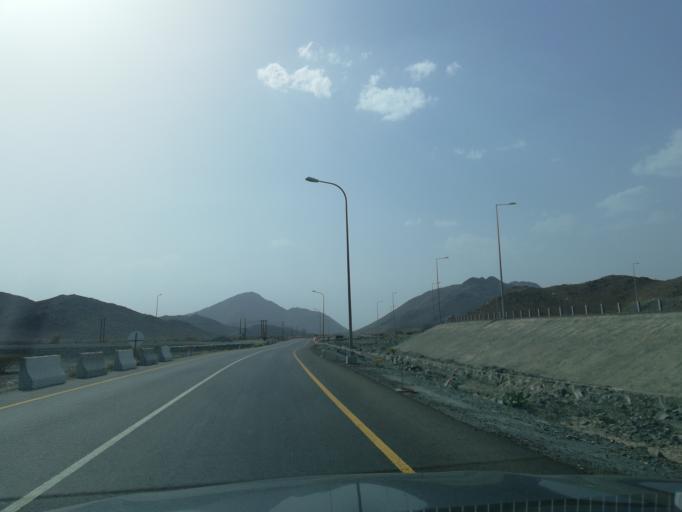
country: OM
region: Muhafazat ad Dakhiliyah
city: Sufalat Sama'il
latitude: 23.0998
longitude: 58.1703
